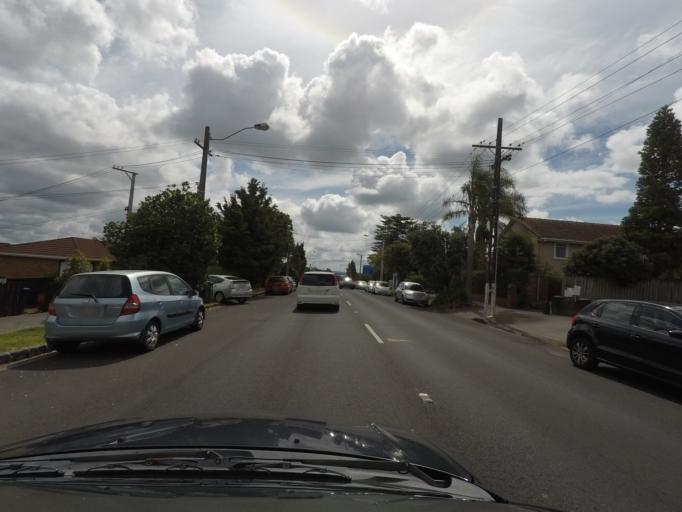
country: NZ
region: Auckland
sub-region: Auckland
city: Rosebank
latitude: -36.8903
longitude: 174.7114
